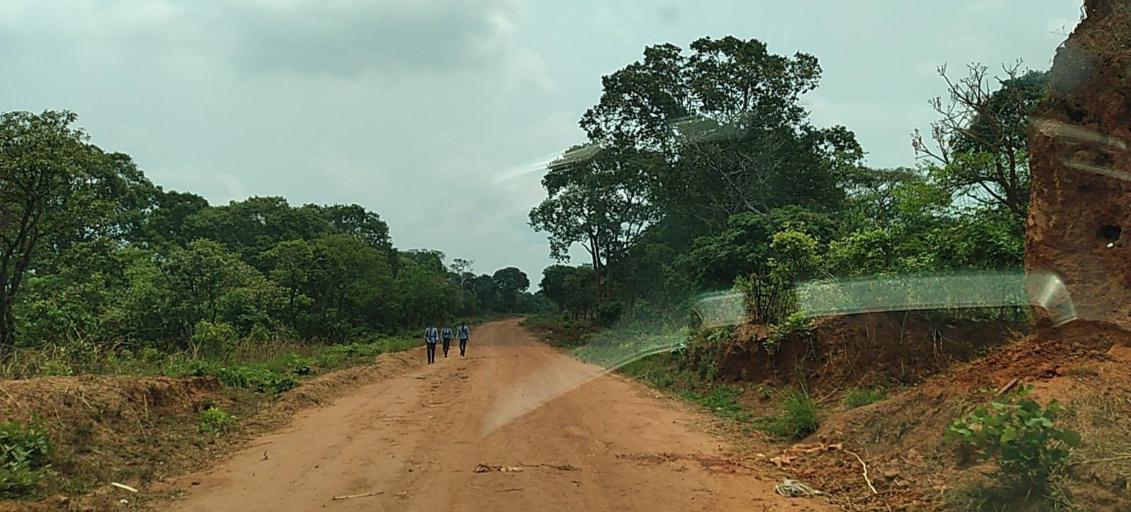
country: ZM
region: North-Western
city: Mwinilunga
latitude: -11.4547
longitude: 24.7564
